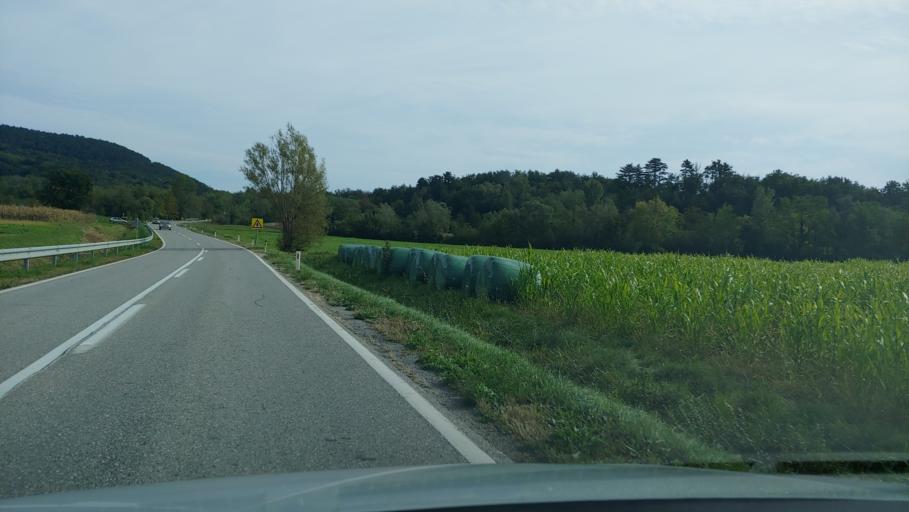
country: SI
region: Nova Gorica
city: Sempas
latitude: 45.9188
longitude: 13.7594
